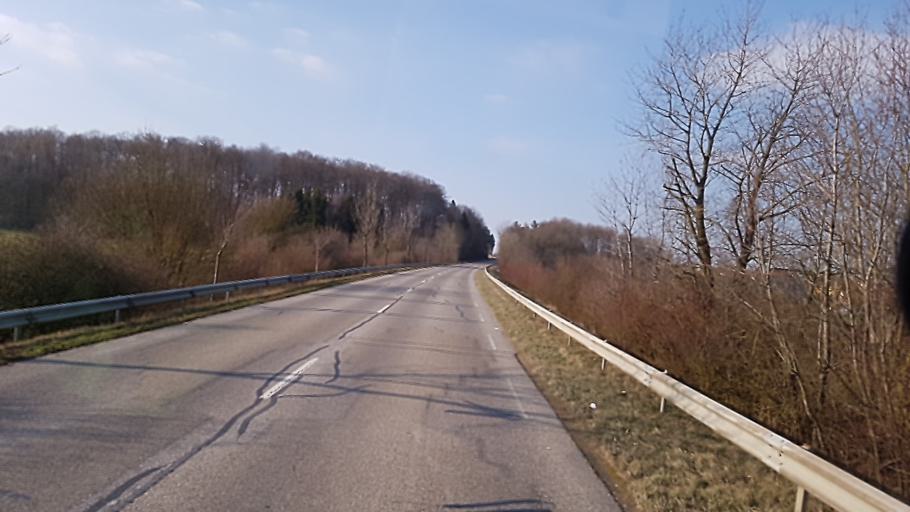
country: FR
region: Alsace
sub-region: Departement du Bas-Rhin
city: Drulingen
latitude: 48.8750
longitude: 7.1601
